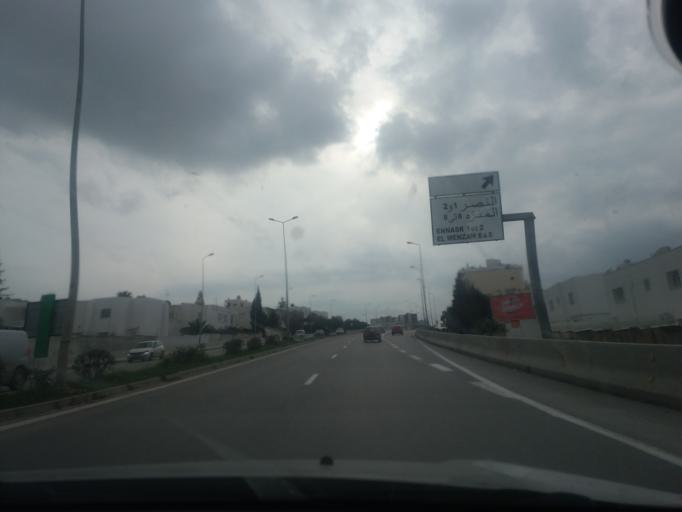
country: TN
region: Ariana
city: Ariana
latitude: 36.8598
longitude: 10.1704
